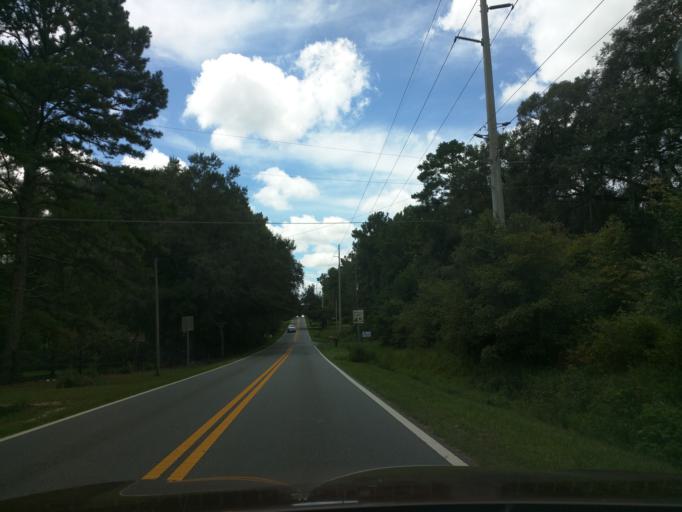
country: US
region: Florida
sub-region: Leon County
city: Tallahassee
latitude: 30.5518
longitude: -84.1764
